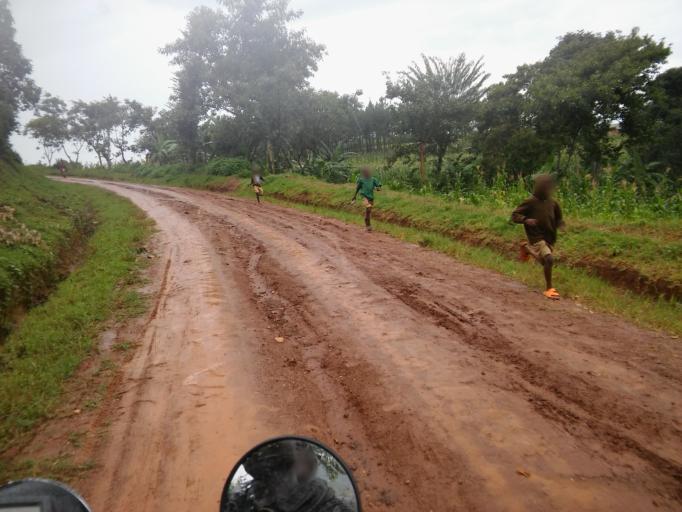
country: UG
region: Eastern Region
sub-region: Bududa District
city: Bududa
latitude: 0.9994
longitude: 34.2495
